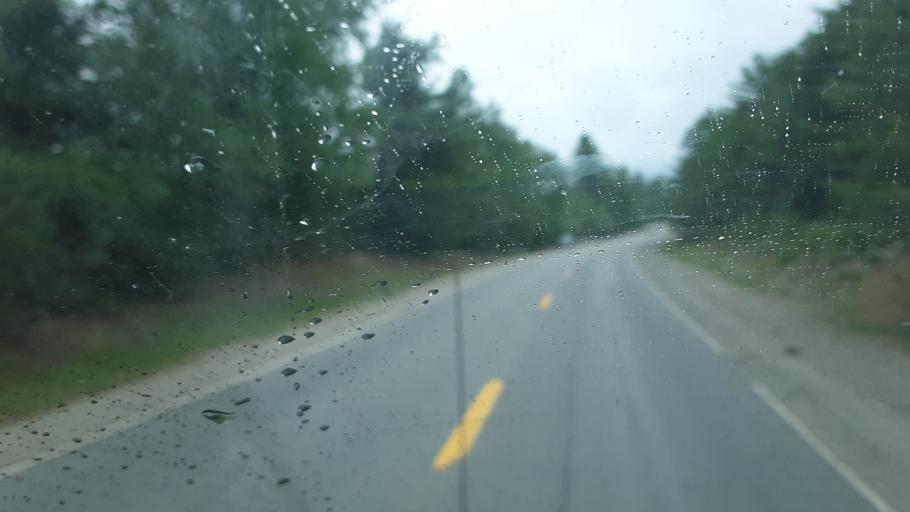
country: US
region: Maine
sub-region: Penobscot County
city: Millinocket
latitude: 45.6927
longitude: -68.7927
